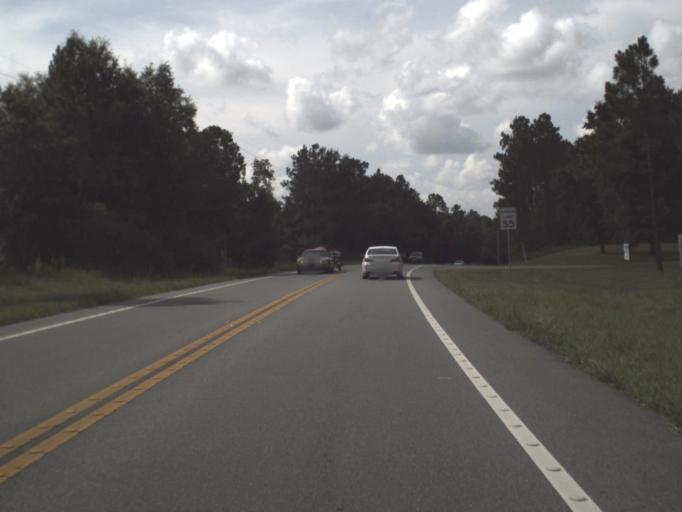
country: US
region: Florida
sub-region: Citrus County
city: Citrus Springs
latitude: 29.0153
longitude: -82.4552
